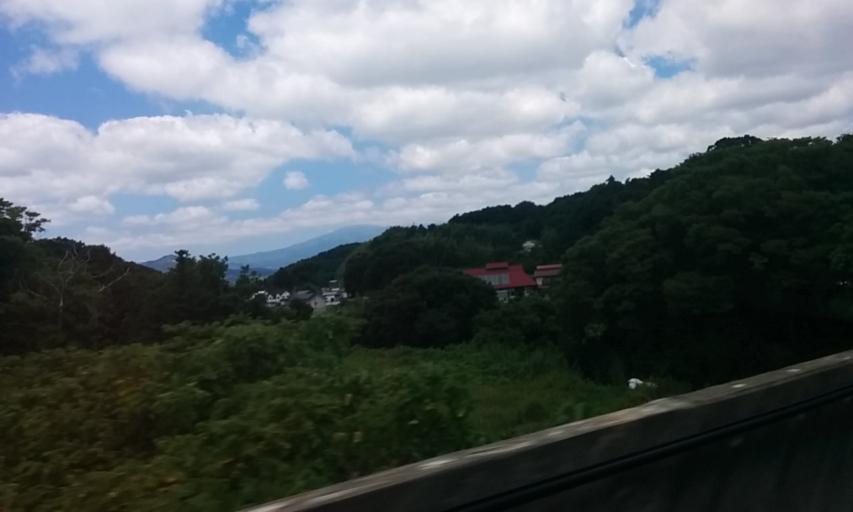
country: JP
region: Fukushima
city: Motomiya
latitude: 37.4804
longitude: 140.4177
